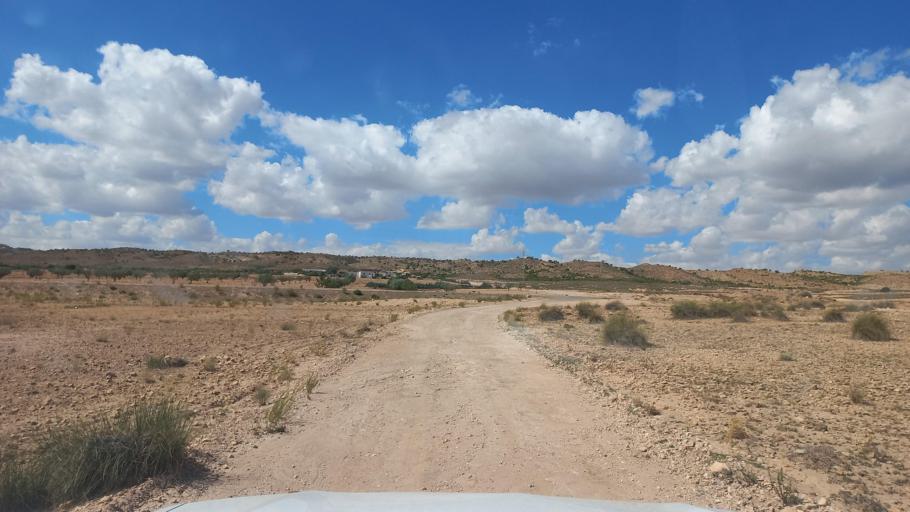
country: TN
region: Al Qasrayn
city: Sbiba
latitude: 35.3622
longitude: 9.0023
